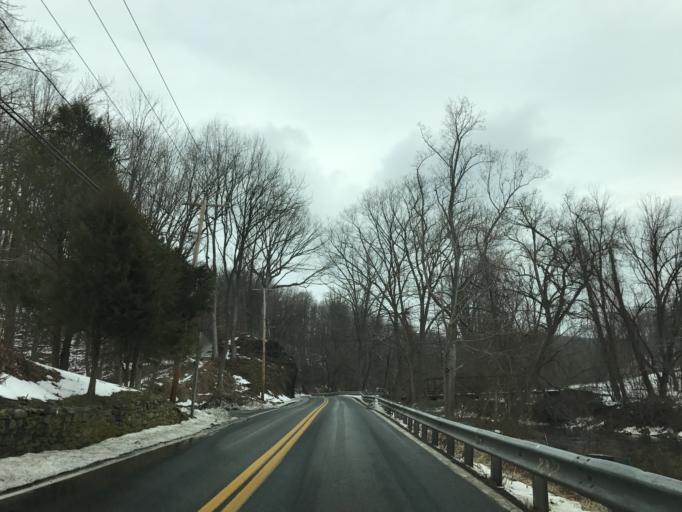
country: US
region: Maryland
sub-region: Harford County
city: Bel Air North
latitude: 39.6229
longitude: -76.4010
